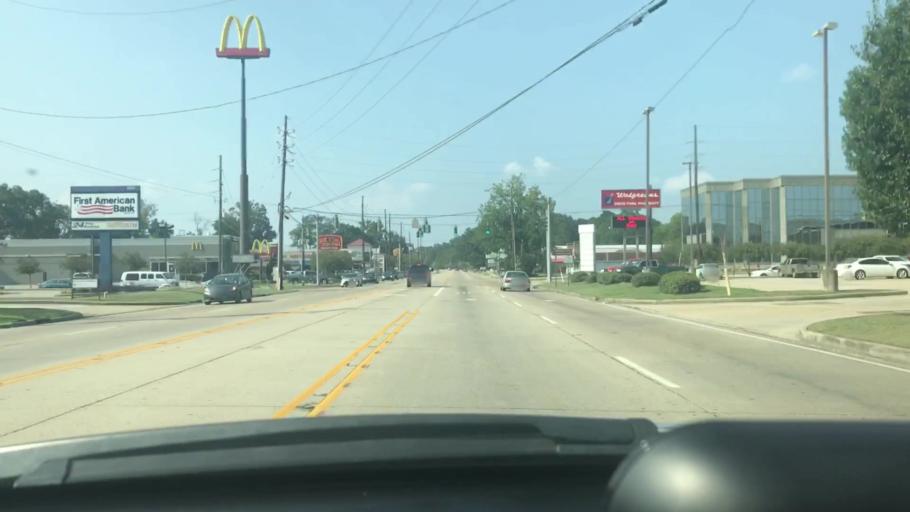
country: US
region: Louisiana
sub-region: Tangipahoa Parish
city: Hammond
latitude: 30.4839
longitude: -90.4569
